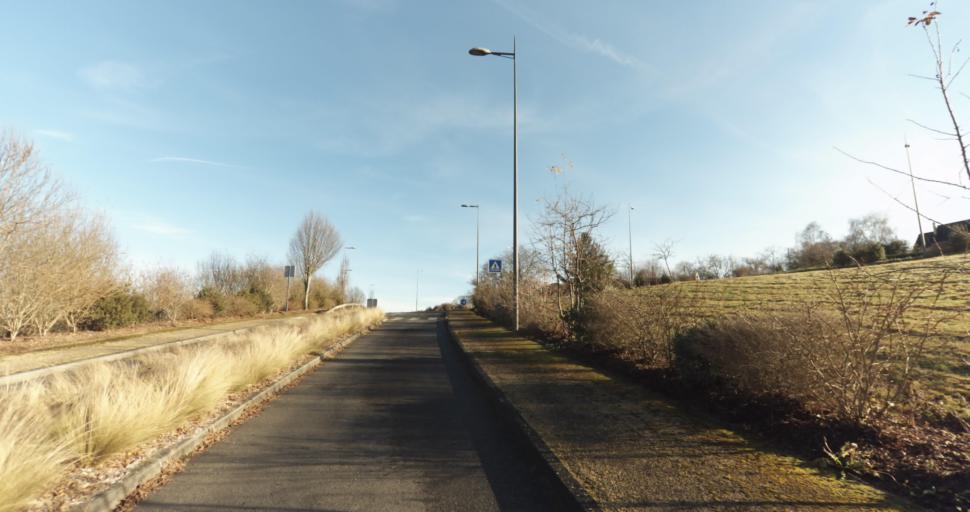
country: FR
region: Limousin
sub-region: Departement de la Haute-Vienne
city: Aixe-sur-Vienne
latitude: 45.7975
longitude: 1.1190
